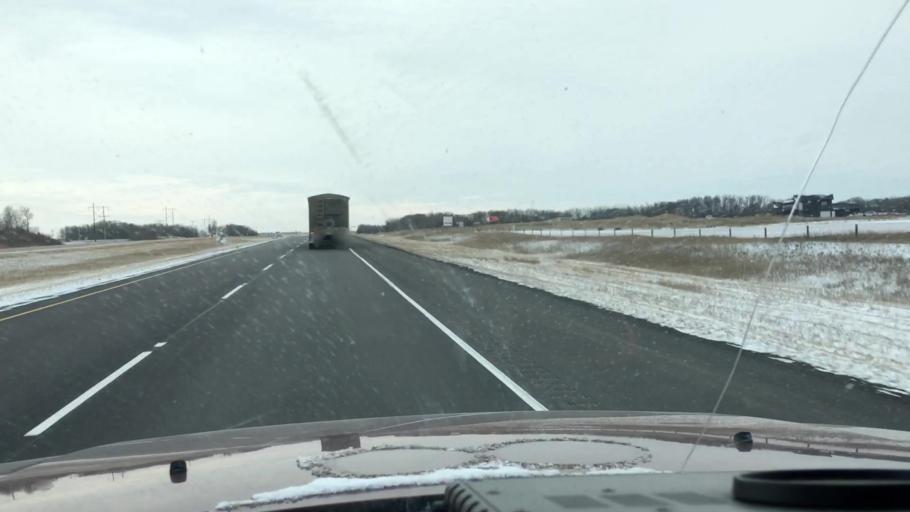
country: CA
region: Saskatchewan
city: Saskatoon
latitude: 51.9448
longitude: -106.5423
